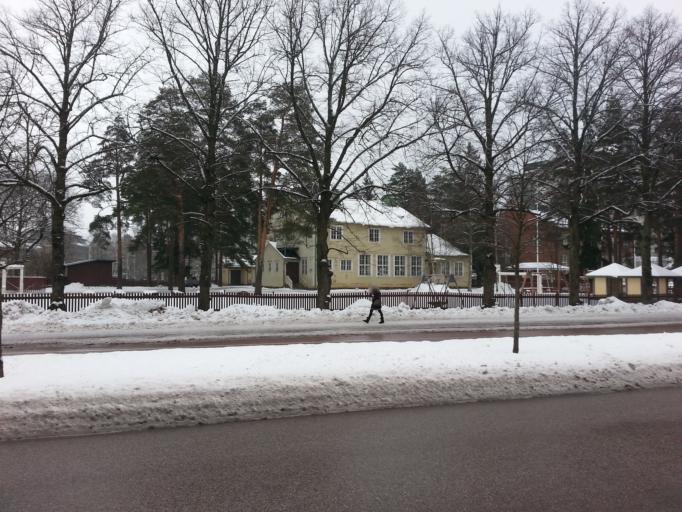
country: FI
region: Uusimaa
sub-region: Helsinki
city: Teekkarikylae
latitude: 60.2286
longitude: 24.8492
